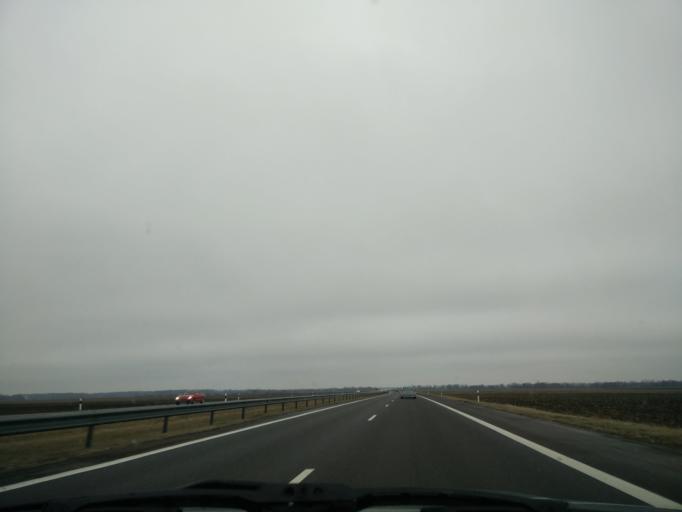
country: LT
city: Raseiniai
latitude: 55.3597
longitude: 23.0198
